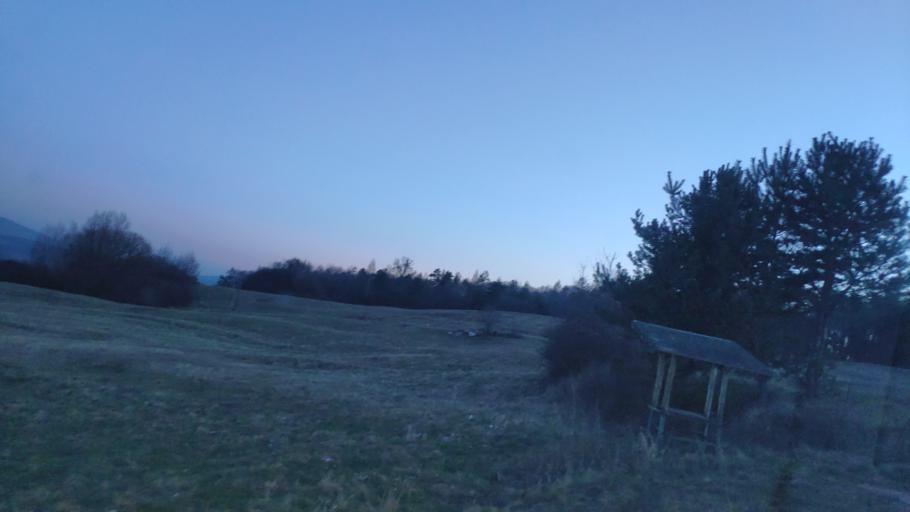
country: SK
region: Kosicky
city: Kosice
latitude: 48.8342
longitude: 21.2561
